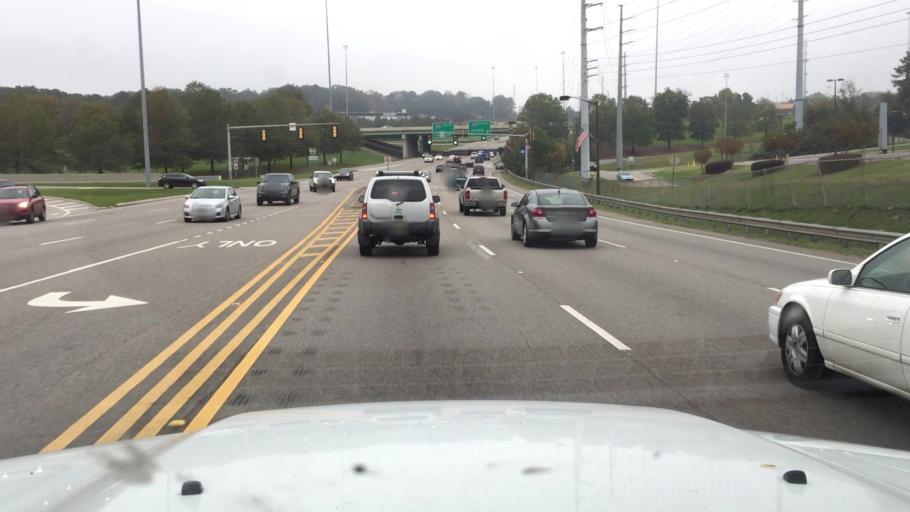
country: US
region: Alabama
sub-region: Jefferson County
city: Hoover
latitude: 33.3817
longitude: -86.8059
